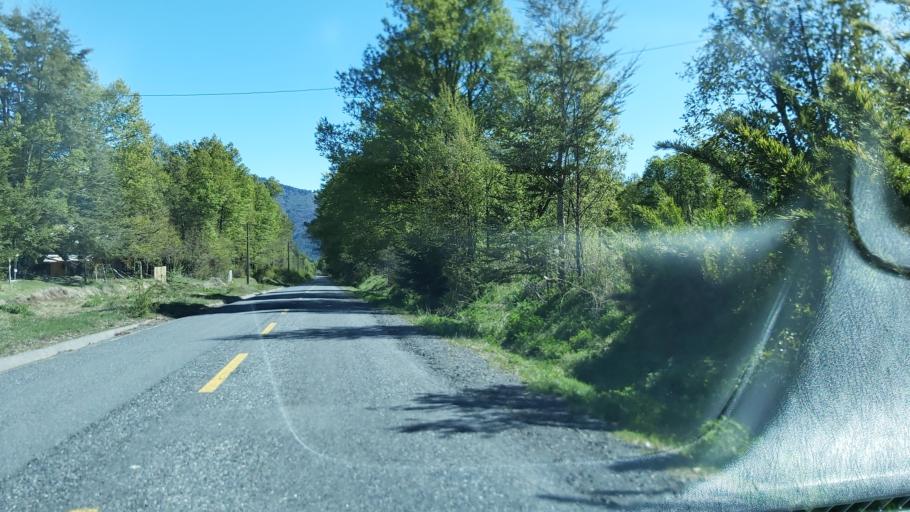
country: CL
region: Araucania
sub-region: Provincia de Cautin
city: Vilcun
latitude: -38.4689
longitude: -71.5227
